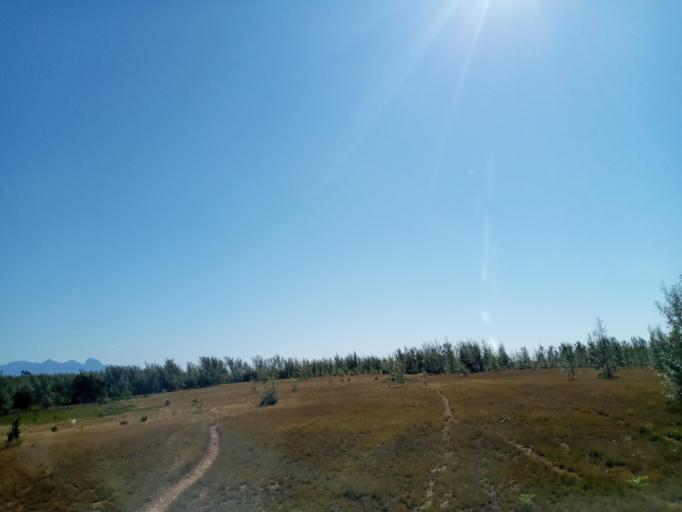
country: MG
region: Atsimo-Atsinanana
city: Vohipaho
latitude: -24.2468
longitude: 47.3158
